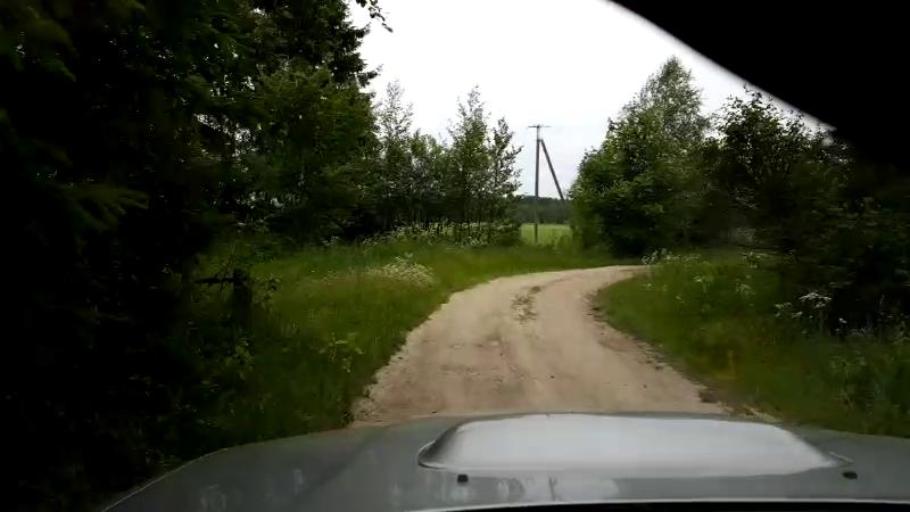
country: EE
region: Paernumaa
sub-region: Halinga vald
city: Parnu-Jaagupi
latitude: 58.5621
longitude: 24.6233
